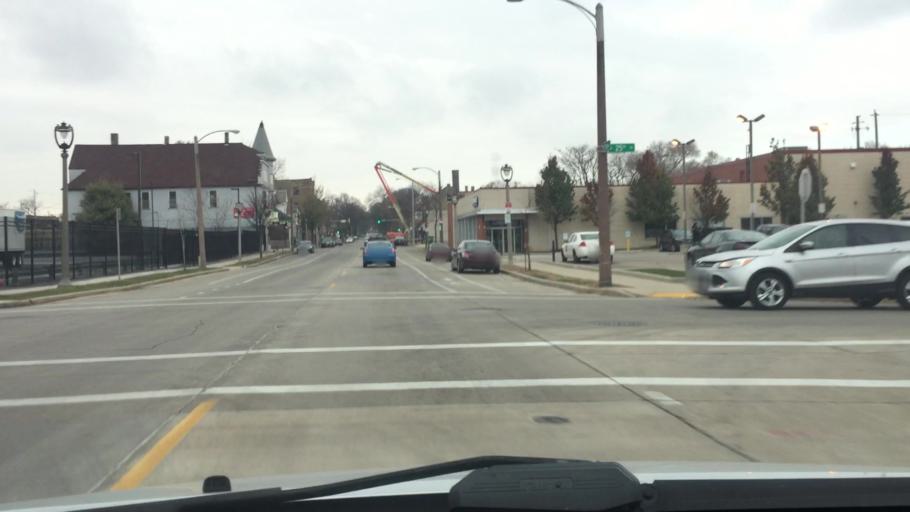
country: US
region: Wisconsin
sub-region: Milwaukee County
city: Milwaukee
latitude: 43.0433
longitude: -87.9448
